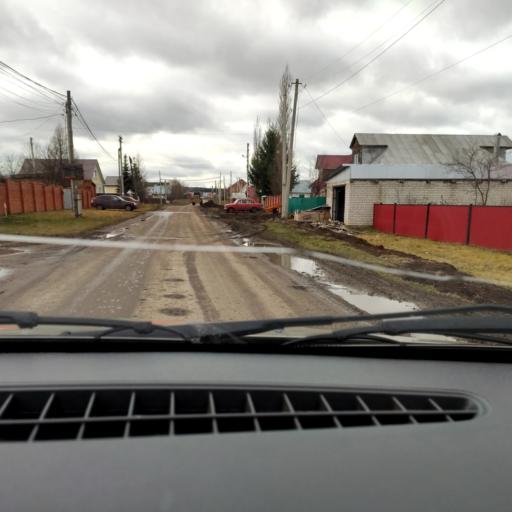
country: RU
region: Bashkortostan
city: Avdon
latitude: 54.4939
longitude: 55.8657
